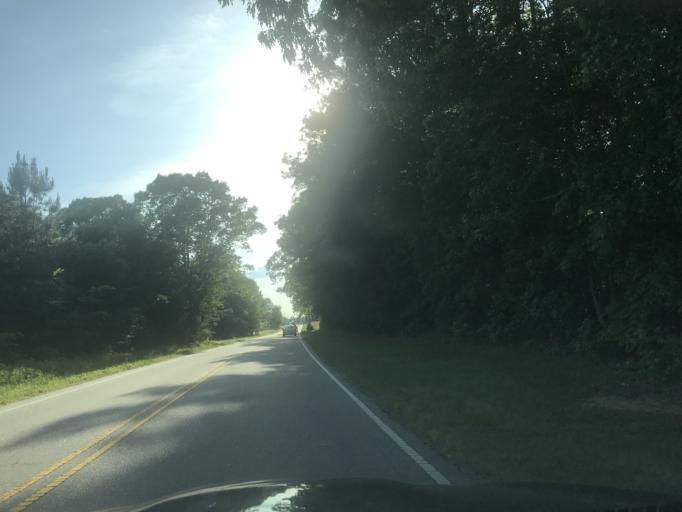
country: US
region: North Carolina
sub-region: Wake County
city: Knightdale
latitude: 35.7469
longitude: -78.4436
